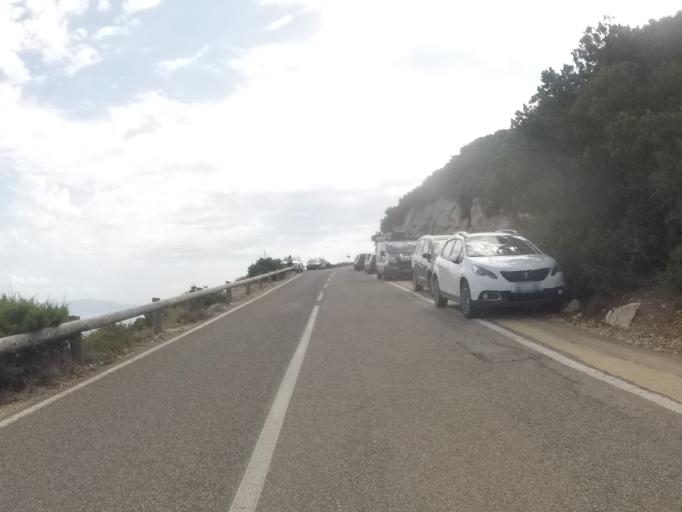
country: IT
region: Sardinia
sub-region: Provincia di Sassari
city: Alghero
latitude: 40.5700
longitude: 8.1628
